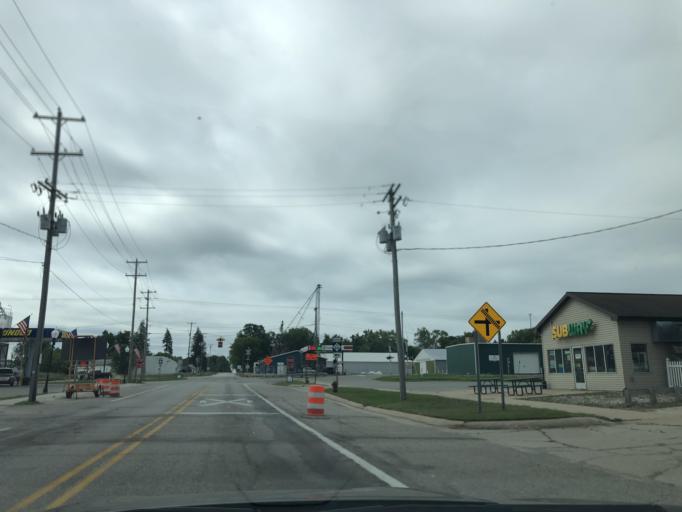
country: US
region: Michigan
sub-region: Missaukee County
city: Lake City
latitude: 44.1947
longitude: -85.2138
